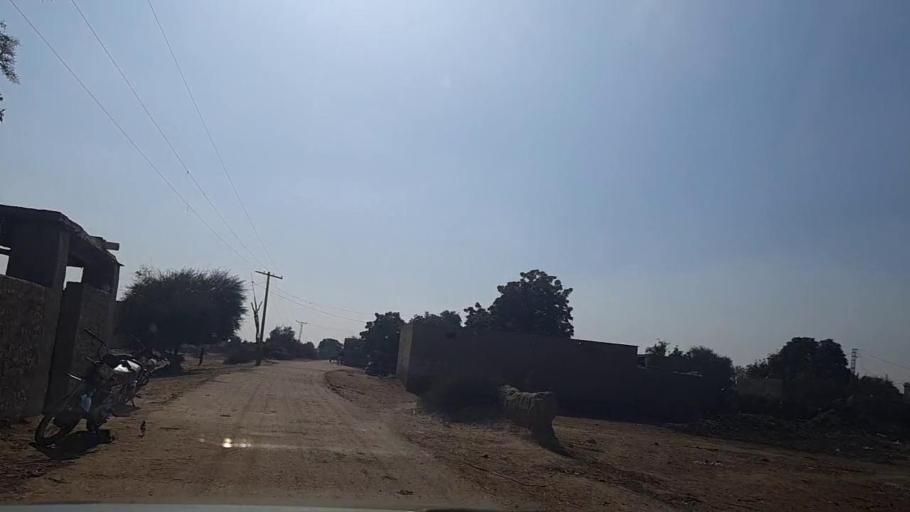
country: PK
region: Sindh
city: Sehwan
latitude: 26.2746
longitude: 68.0360
